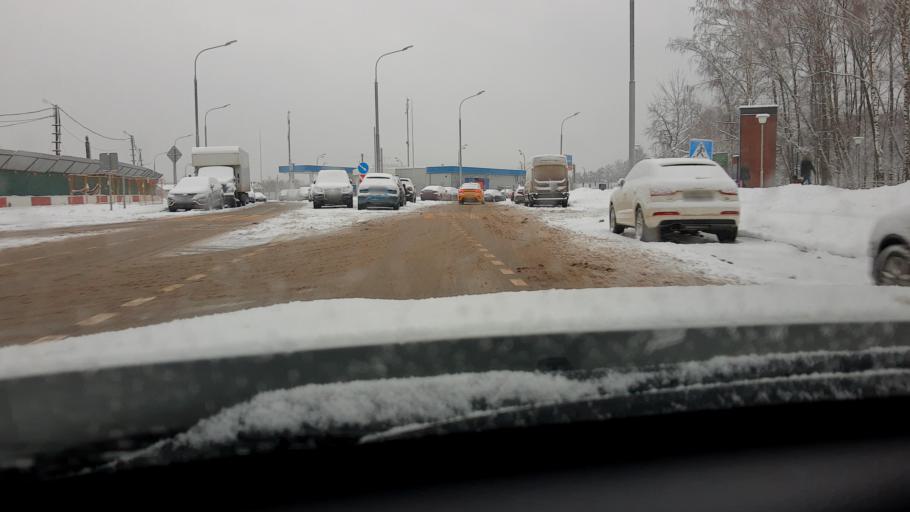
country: RU
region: Moscow
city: Novo-Peredelkino
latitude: 55.6327
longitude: 37.3216
